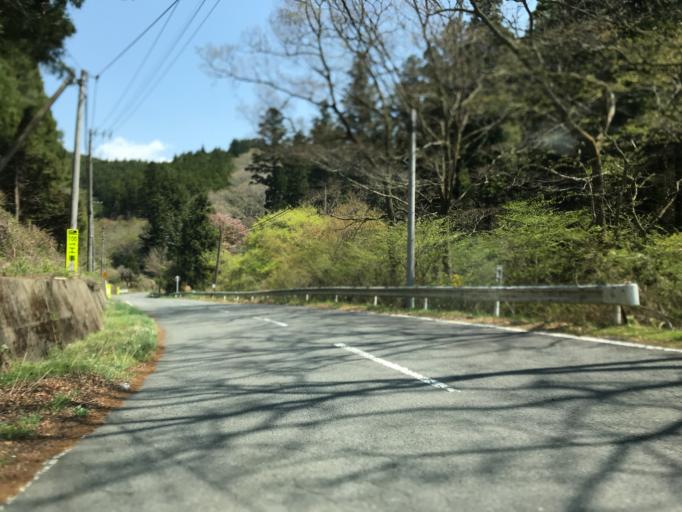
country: JP
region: Ibaraki
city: Kitaibaraki
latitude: 36.9646
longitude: 140.6636
